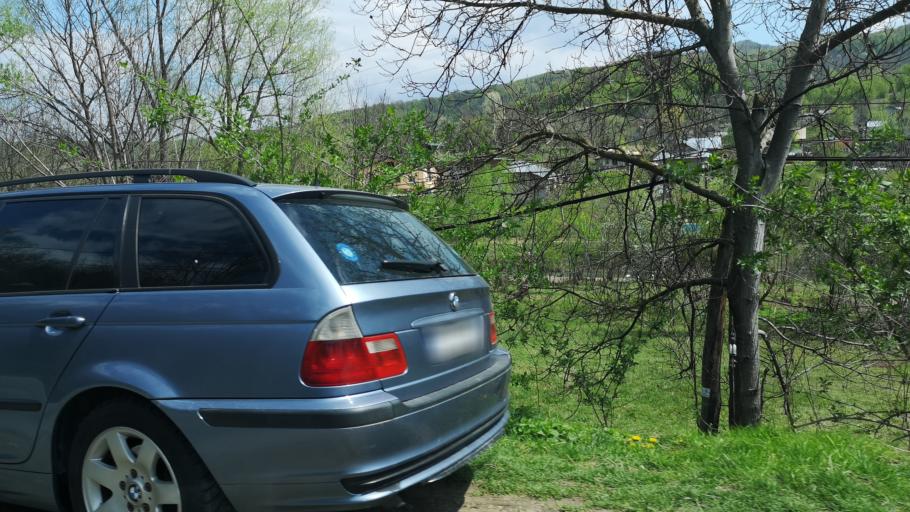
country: RO
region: Prahova
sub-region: Comuna Soimari
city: Soimari
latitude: 45.1601
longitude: 26.2051
